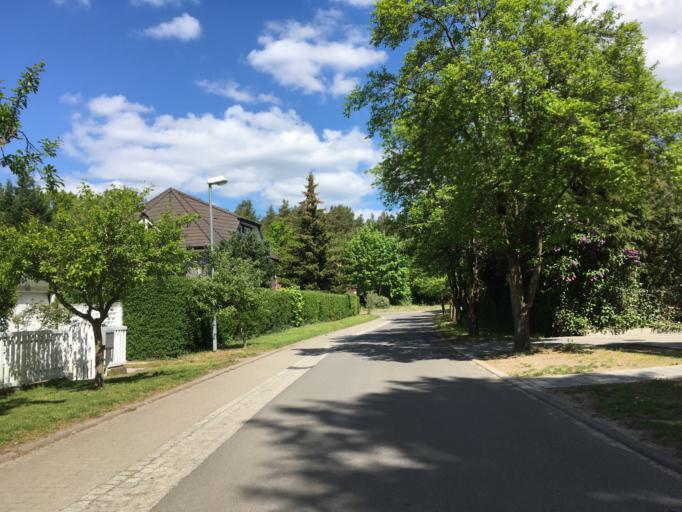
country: DE
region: Brandenburg
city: Glienicke
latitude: 52.6754
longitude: 13.3688
